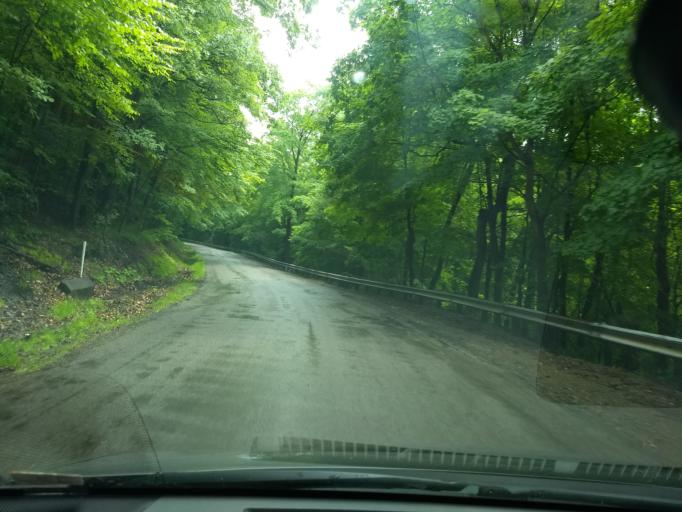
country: US
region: Pennsylvania
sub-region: Armstrong County
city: Orchard Hills
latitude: 40.5649
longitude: -79.5146
